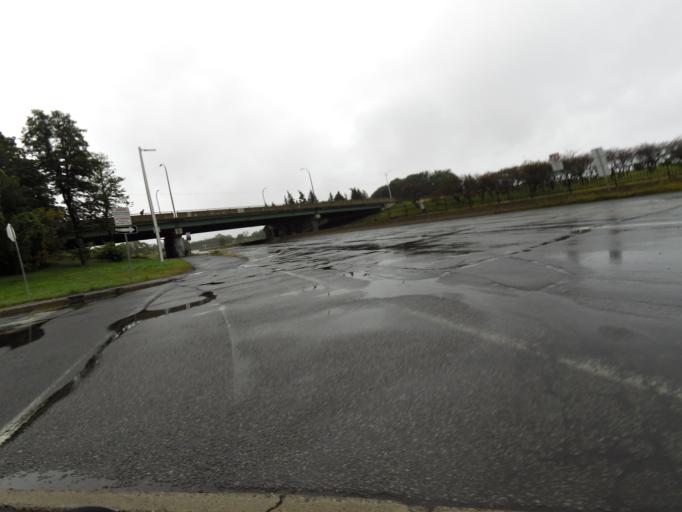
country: CA
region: Ontario
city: Bells Corners
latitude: 45.3655
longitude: -75.7832
